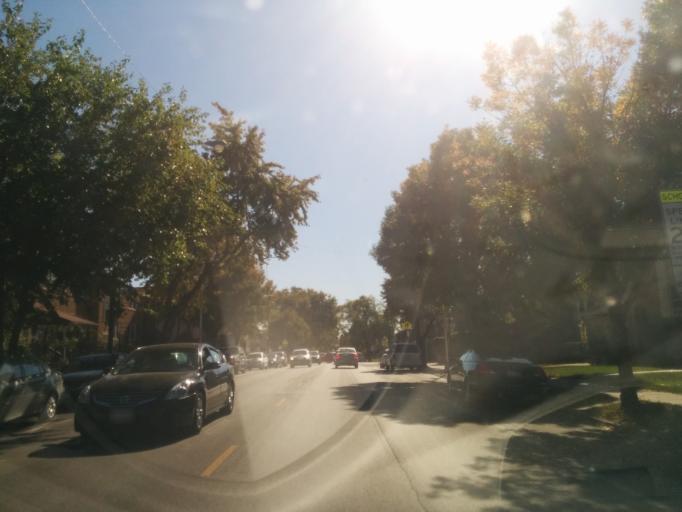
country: US
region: Illinois
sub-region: Cook County
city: Elmwood Park
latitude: 41.9372
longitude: -87.7859
